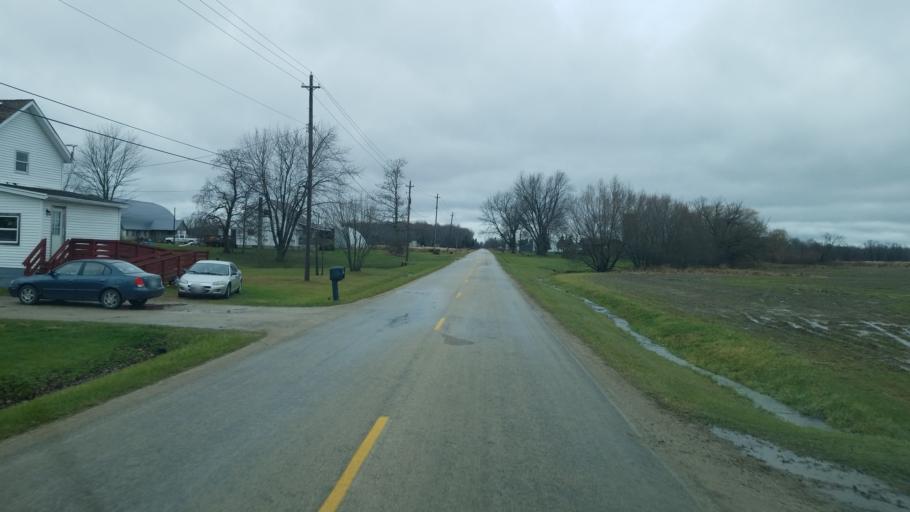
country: US
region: Ohio
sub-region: Ashtabula County
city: Jefferson
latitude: 41.7700
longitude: -80.6231
